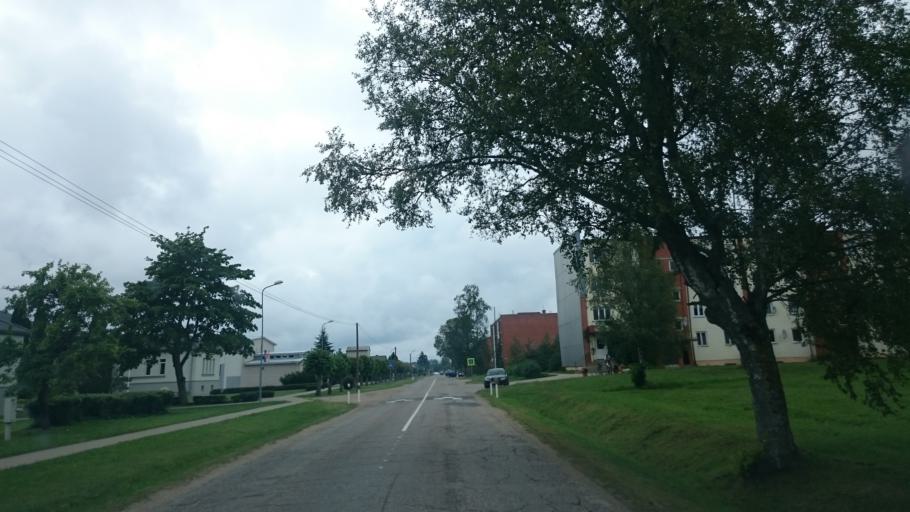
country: LV
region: Pavilostas
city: Pavilosta
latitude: 56.8829
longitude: 21.2044
